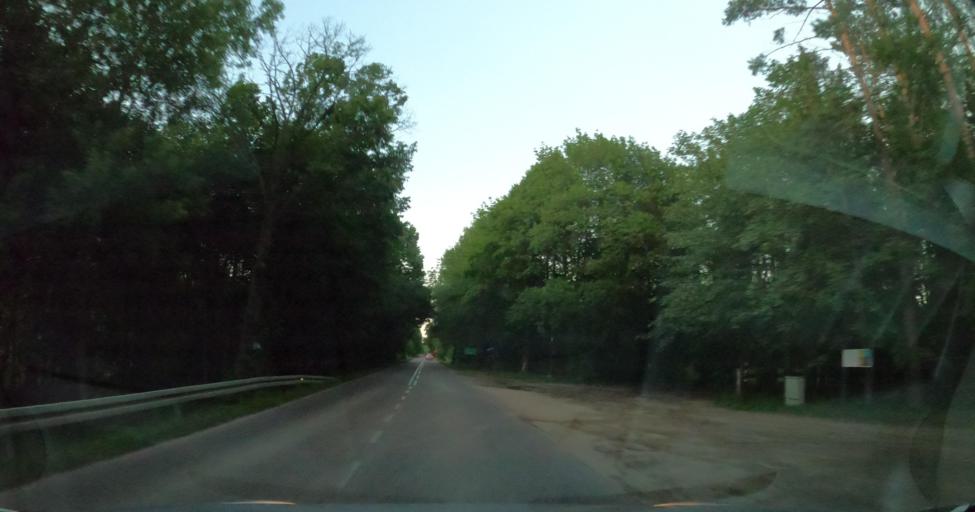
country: PL
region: Pomeranian Voivodeship
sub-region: Powiat wejherowski
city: Linia
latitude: 54.4605
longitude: 18.0528
